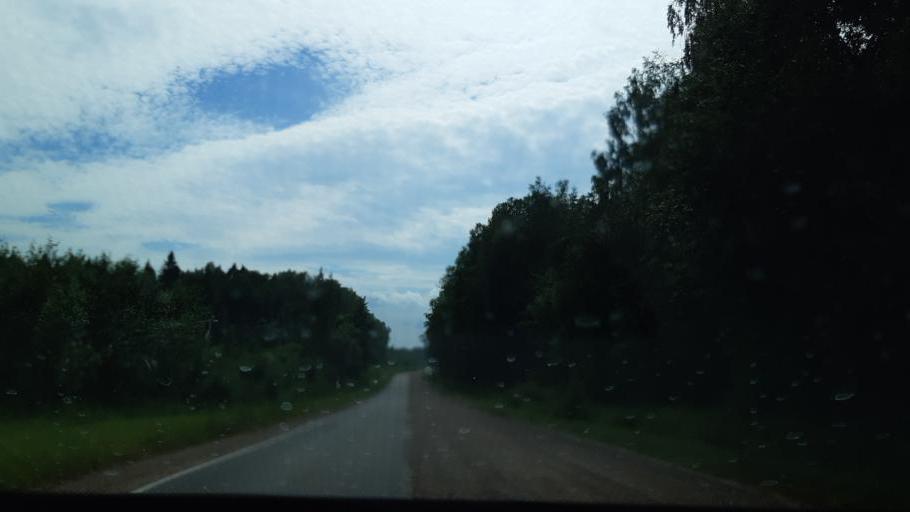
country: RU
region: Moskovskaya
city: Vereya
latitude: 55.2469
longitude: 36.0510
